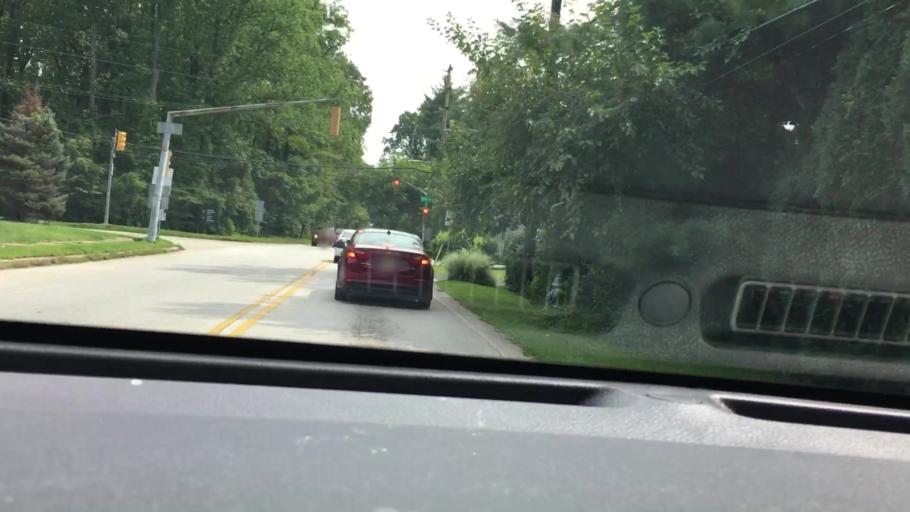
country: US
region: Pennsylvania
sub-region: Bucks County
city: Feasterville
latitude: 40.1343
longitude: -75.0334
